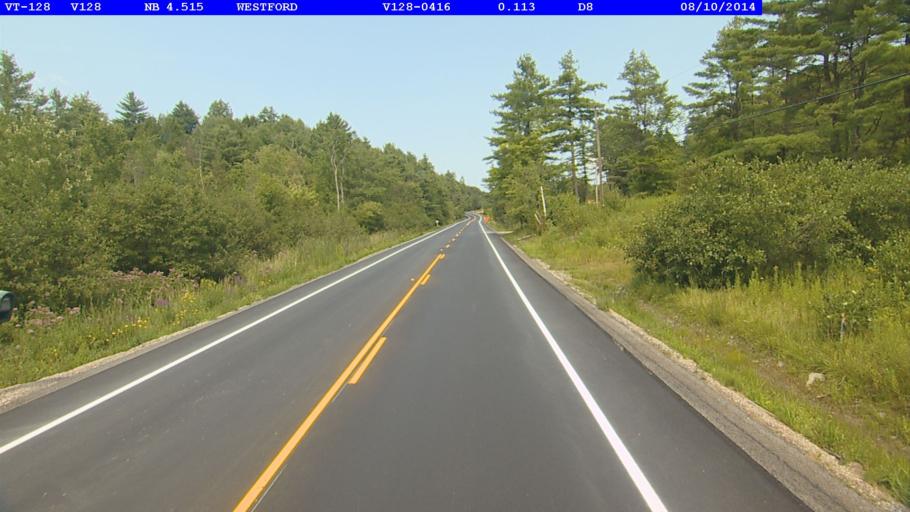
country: US
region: Vermont
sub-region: Chittenden County
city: Jericho
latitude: 44.5609
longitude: -73.0273
